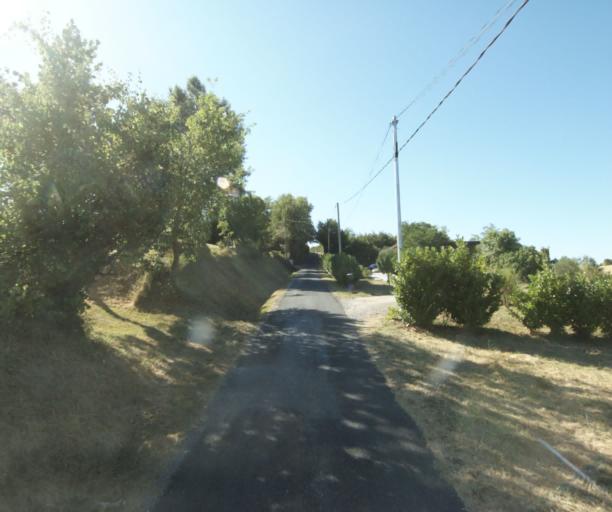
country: FR
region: Midi-Pyrenees
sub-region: Departement de la Haute-Garonne
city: Saint-Felix-Lauragais
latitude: 43.5093
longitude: 1.9400
